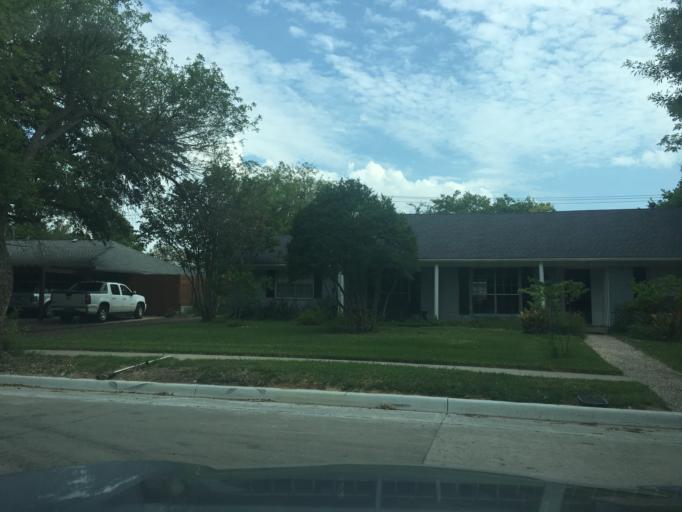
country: US
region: Texas
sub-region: Dallas County
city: Farmers Branch
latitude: 32.9296
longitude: -96.8639
